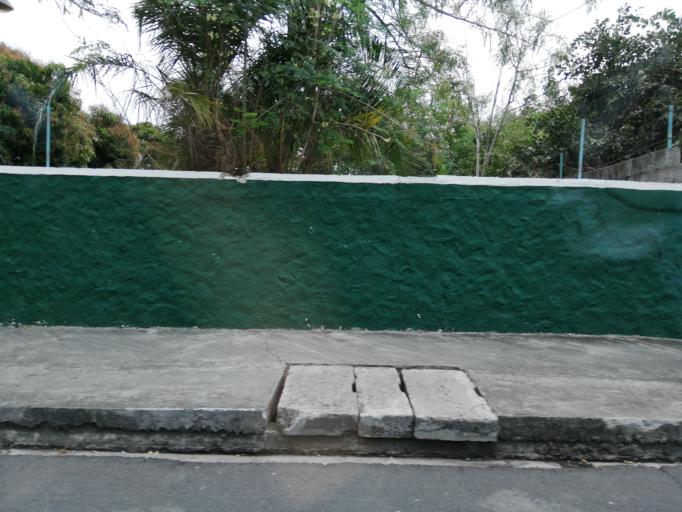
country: MU
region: Port Louis
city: Port Louis
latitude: -20.1635
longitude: 57.4818
